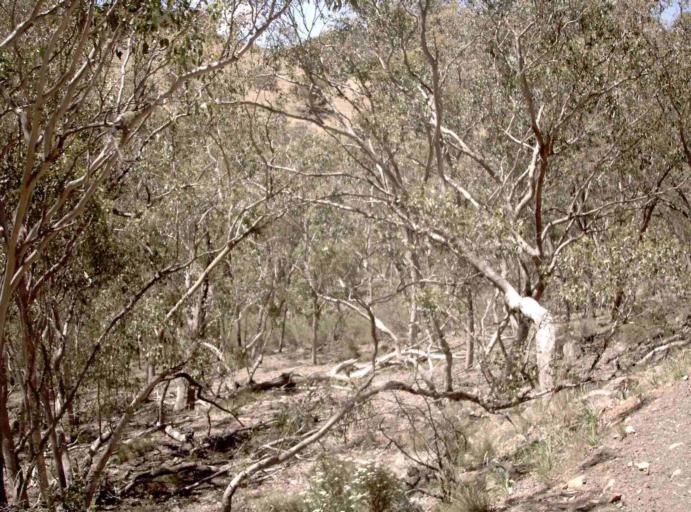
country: AU
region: New South Wales
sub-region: Snowy River
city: Jindabyne
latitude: -37.0748
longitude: 148.4682
